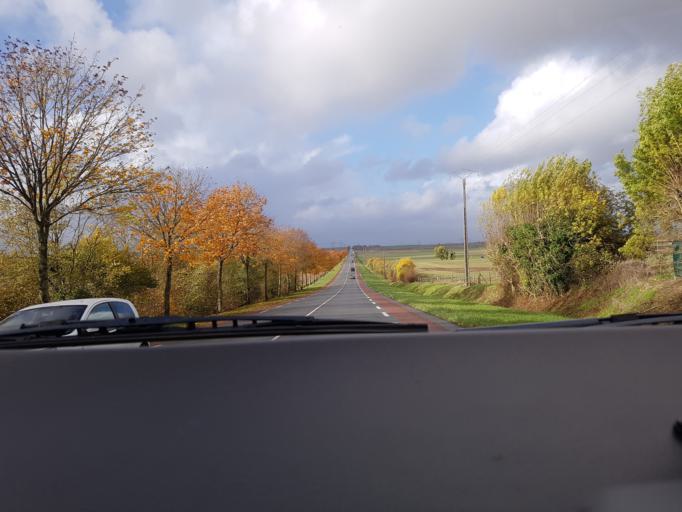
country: FR
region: Poitou-Charentes
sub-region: Departement de la Charente-Maritime
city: Les Gonds
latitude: 45.6555
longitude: -0.5890
